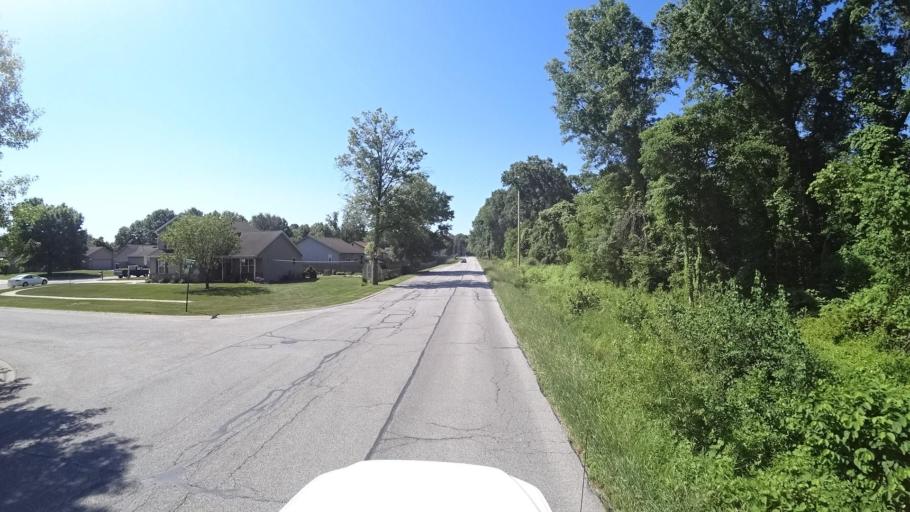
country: US
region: Indiana
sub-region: Porter County
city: Porter
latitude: 41.5966
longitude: -87.1053
